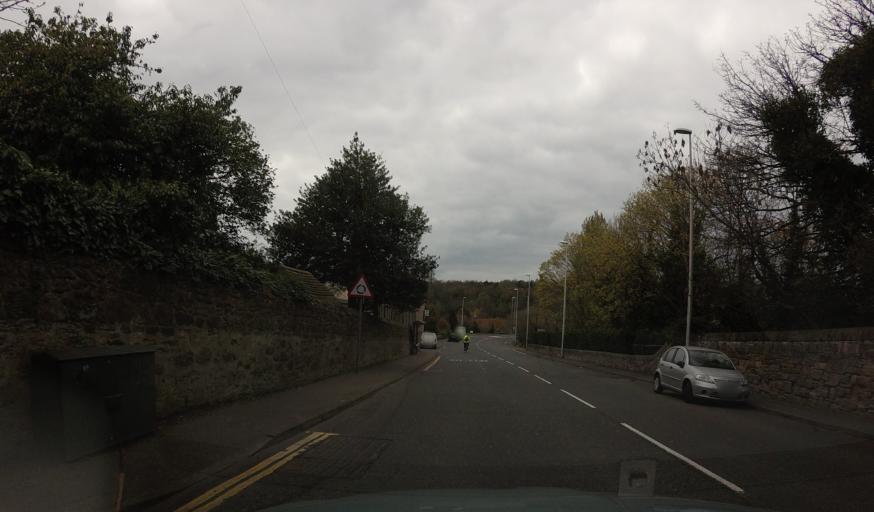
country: GB
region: Scotland
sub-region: Midlothian
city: Dalkeith
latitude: 55.8954
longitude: -3.0715
